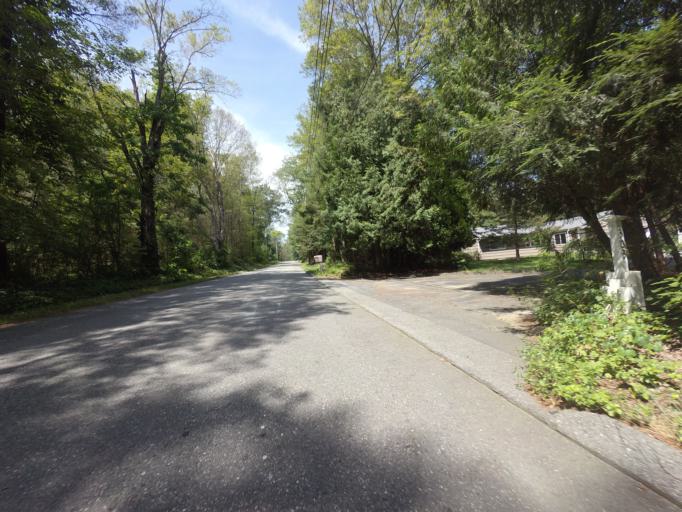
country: US
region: Connecticut
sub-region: Windham County
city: East Brooklyn
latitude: 41.8285
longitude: -71.9340
